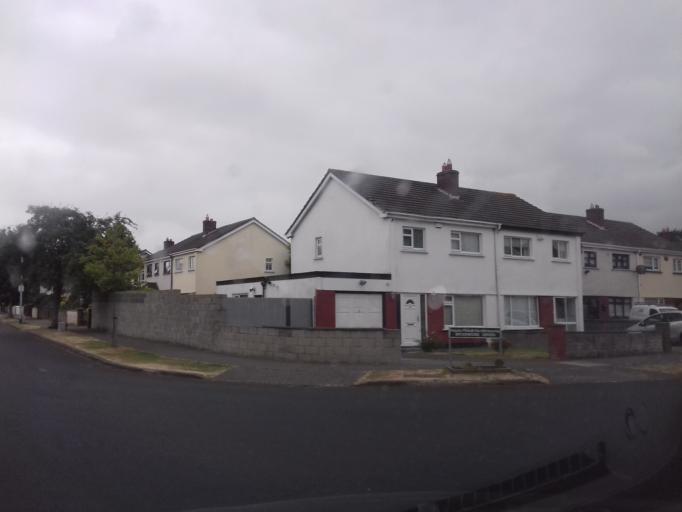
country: IE
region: Leinster
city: Hartstown
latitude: 53.3983
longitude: -6.4049
